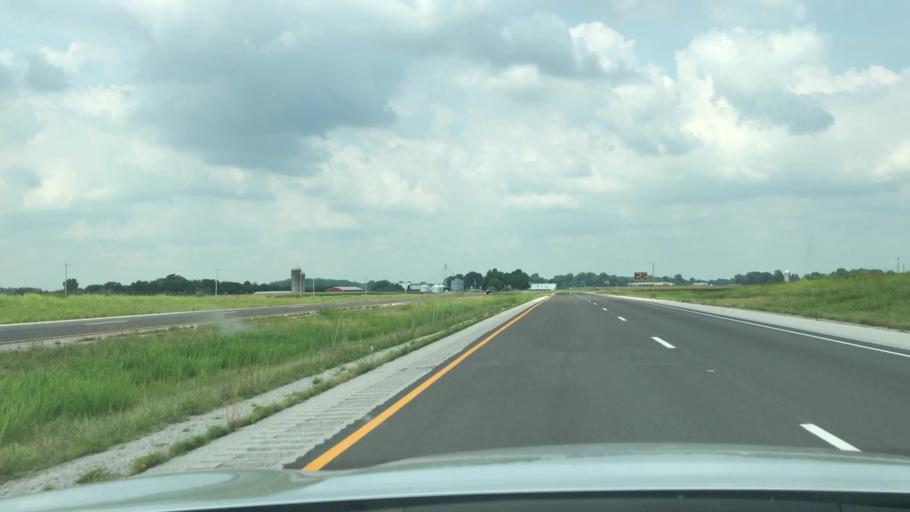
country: US
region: Kentucky
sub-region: Todd County
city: Elkton
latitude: 36.8082
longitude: -87.0466
